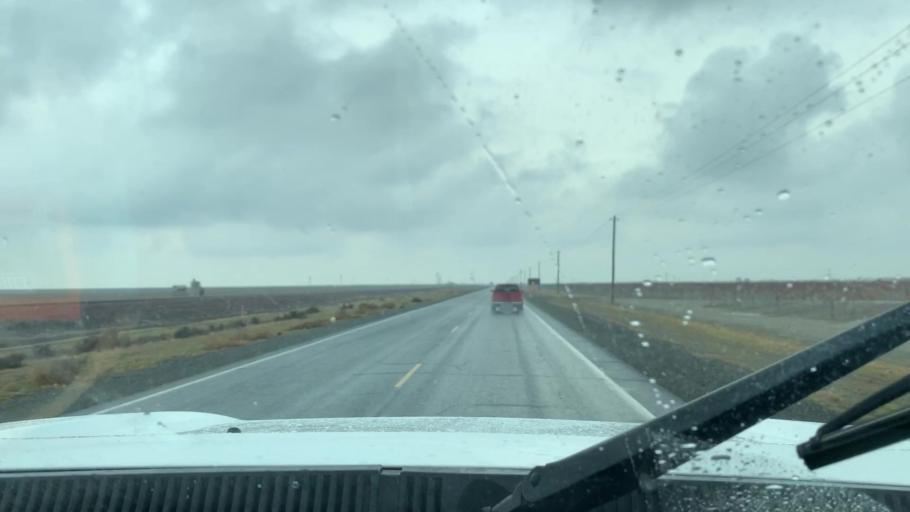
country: US
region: California
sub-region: Tulare County
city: Alpaugh
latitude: 36.0027
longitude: -119.4866
